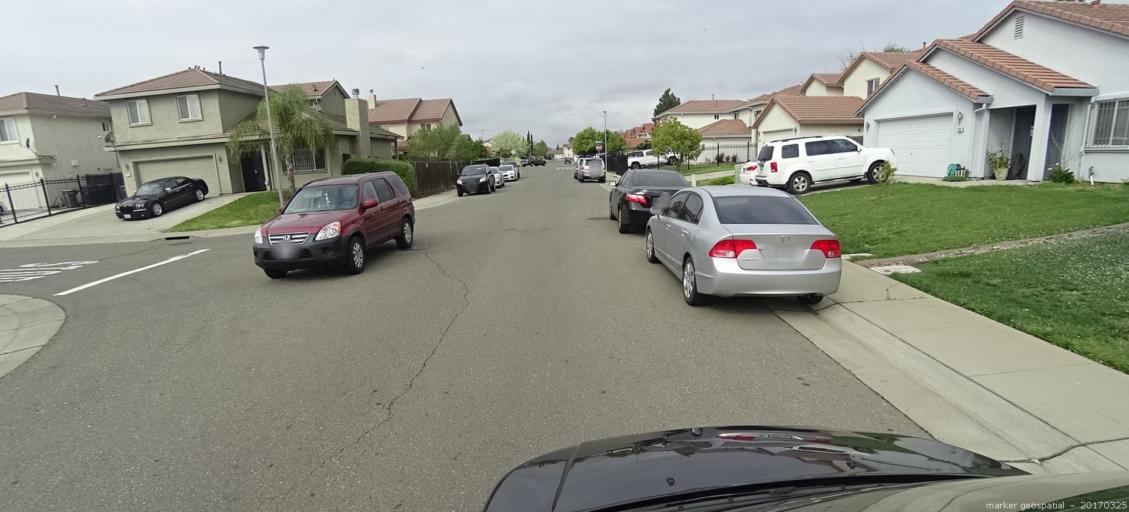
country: US
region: California
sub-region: Sacramento County
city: Florin
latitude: 38.5175
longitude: -121.4189
